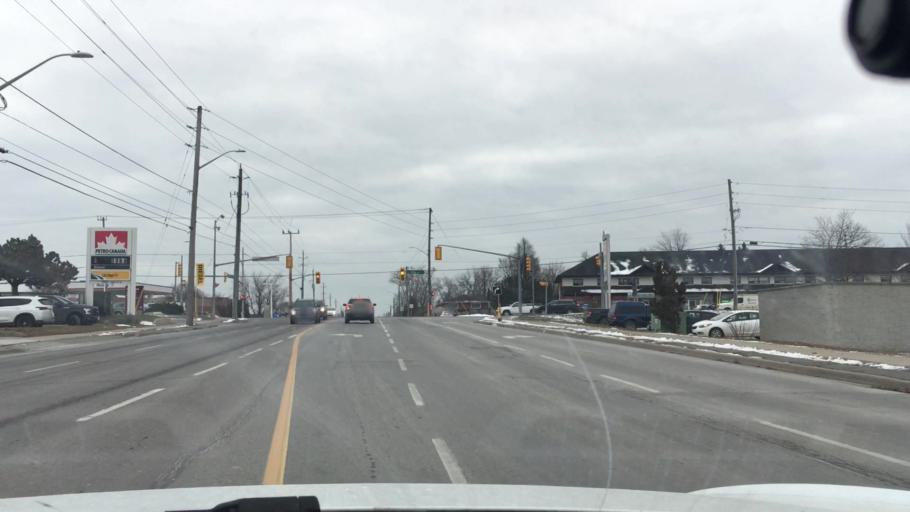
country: CA
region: Ontario
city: Oshawa
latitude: 43.9074
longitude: -78.8138
